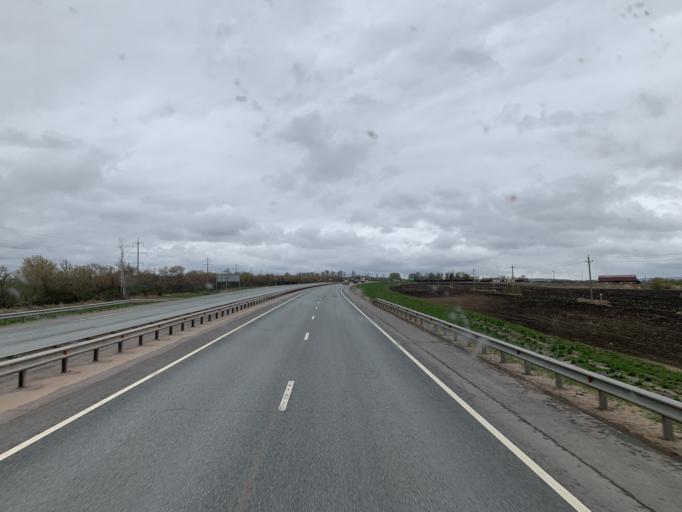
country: RU
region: Ulyanovsk
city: Kanadey
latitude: 53.1306
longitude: 47.4550
